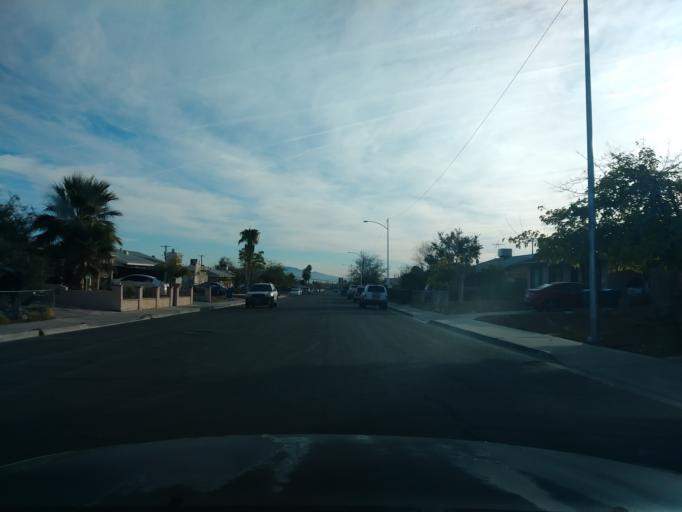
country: US
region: Nevada
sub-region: Clark County
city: Spring Valley
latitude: 36.1615
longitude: -115.2357
